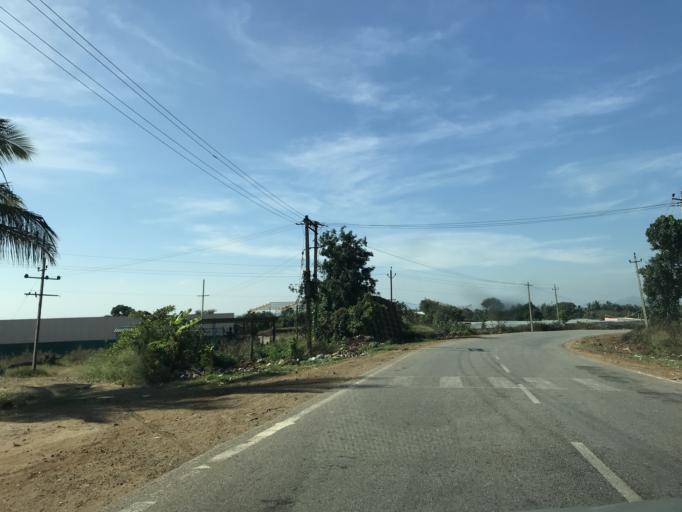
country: IN
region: Karnataka
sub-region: Mysore
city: Sargur
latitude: 12.1327
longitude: 76.5069
